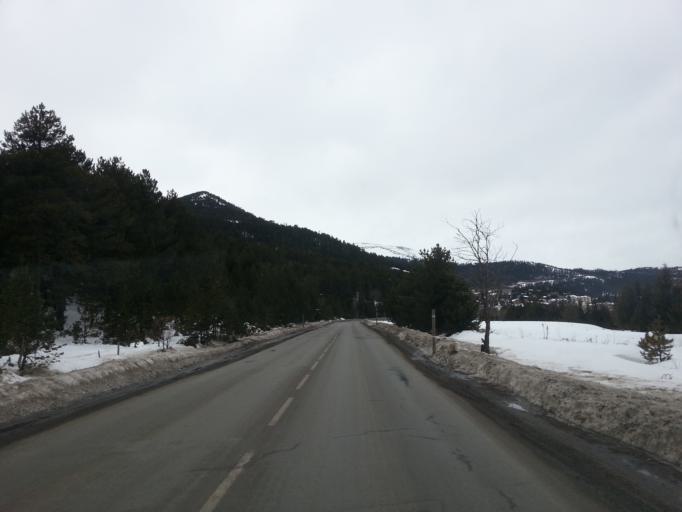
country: ES
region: Catalonia
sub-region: Provincia de Girona
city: Llivia
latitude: 42.5606
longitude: 2.0763
